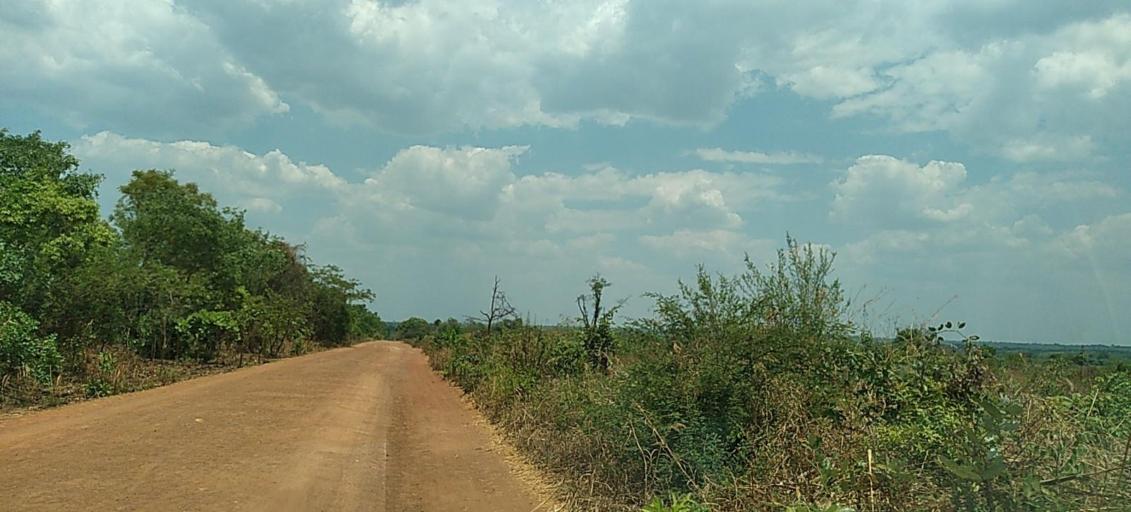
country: ZM
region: Copperbelt
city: Luanshya
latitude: -13.3844
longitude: 28.4404
